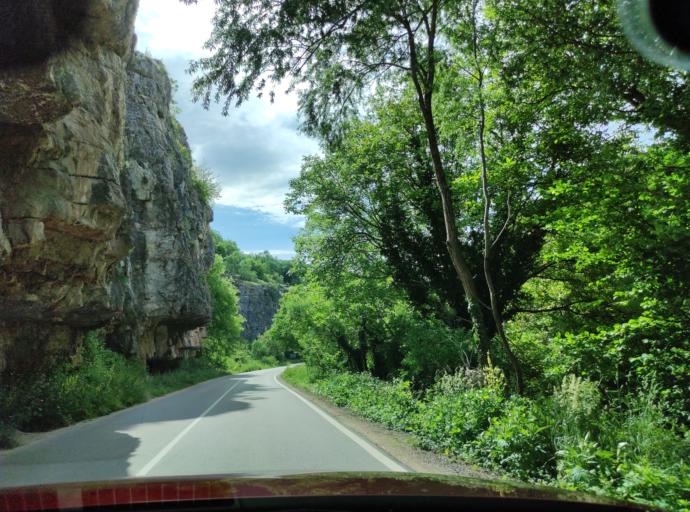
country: BG
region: Montana
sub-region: Obshtina Chiprovtsi
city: Chiprovtsi
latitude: 43.4430
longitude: 22.9327
